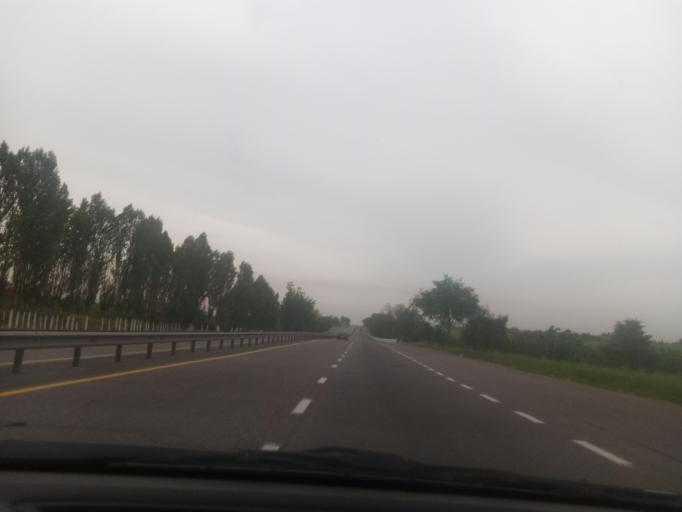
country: UZ
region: Toshkent
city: Tuytepa
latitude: 41.0902
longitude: 69.4632
